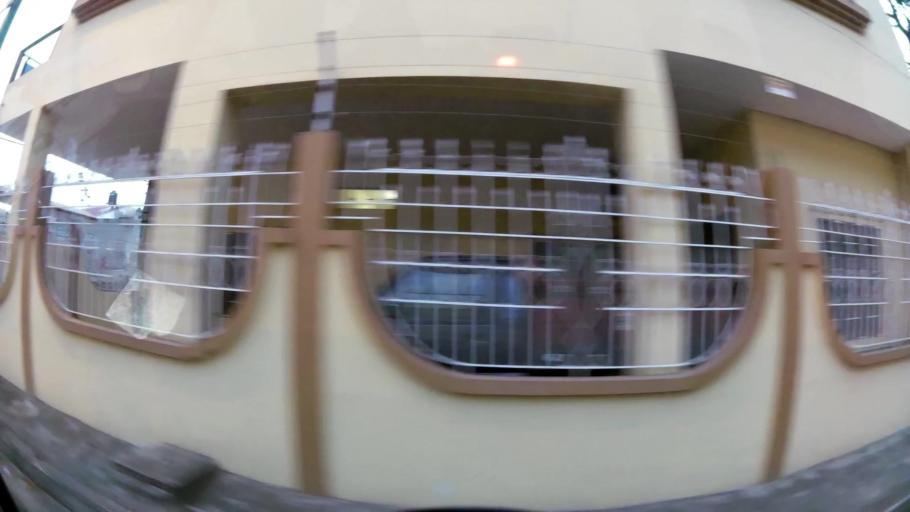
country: EC
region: El Oro
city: Machala
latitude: -3.2665
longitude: -79.9370
